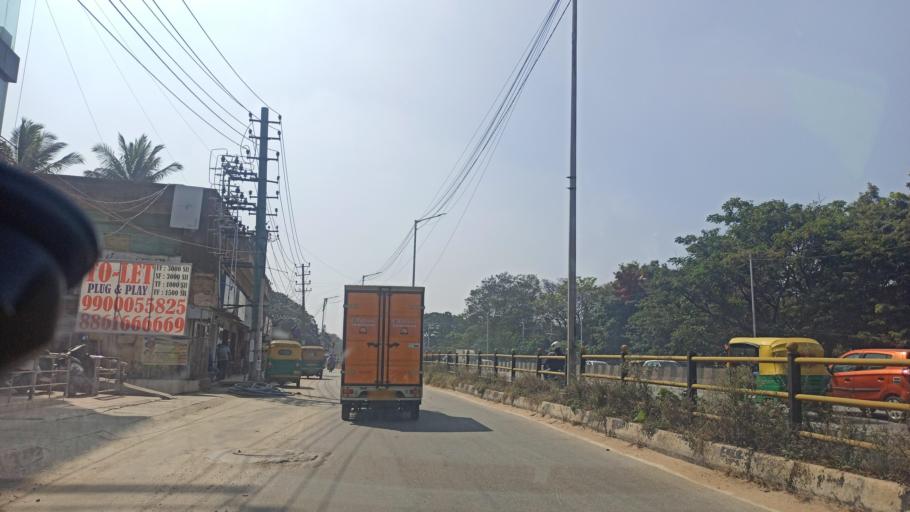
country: IN
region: Karnataka
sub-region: Bangalore Urban
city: Bangalore
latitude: 13.0348
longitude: 77.5887
